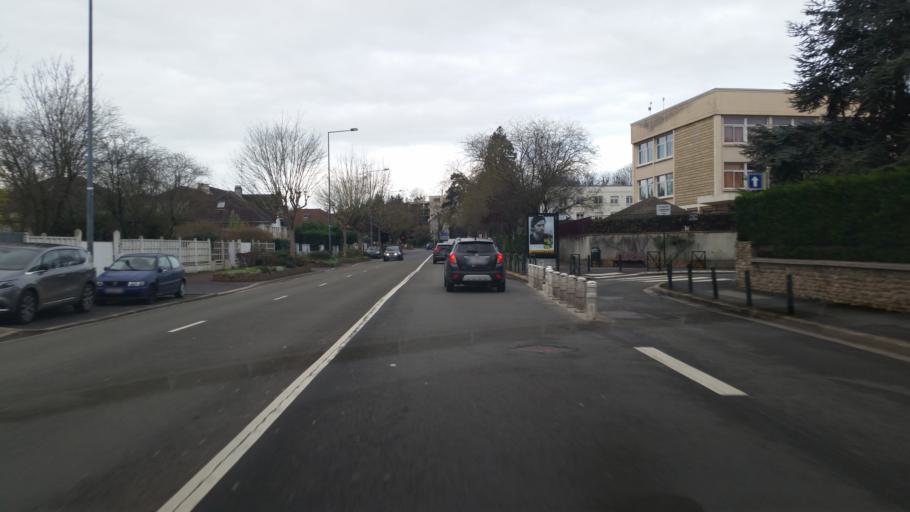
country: FR
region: Ile-de-France
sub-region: Departement des Hauts-de-Seine
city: Vaucresson
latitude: 48.8378
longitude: 2.1597
